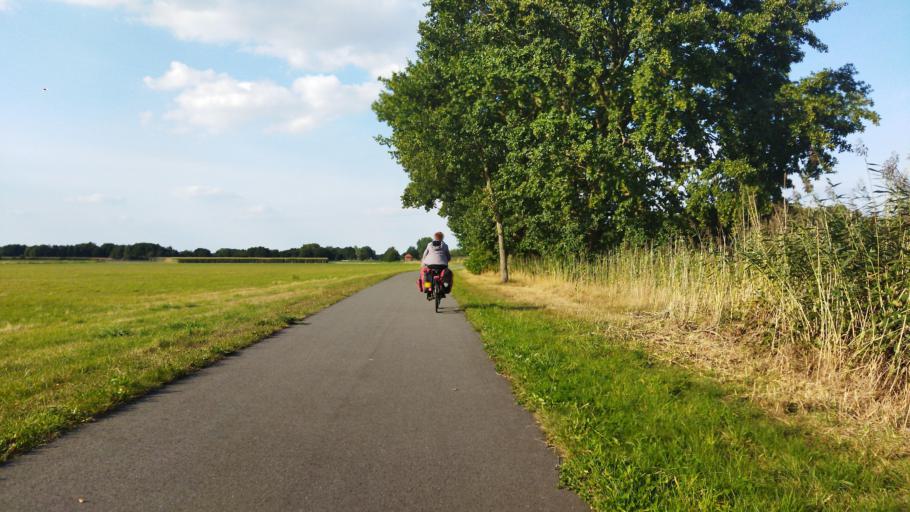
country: DE
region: Lower Saxony
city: Lehe
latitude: 53.0173
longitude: 7.3219
